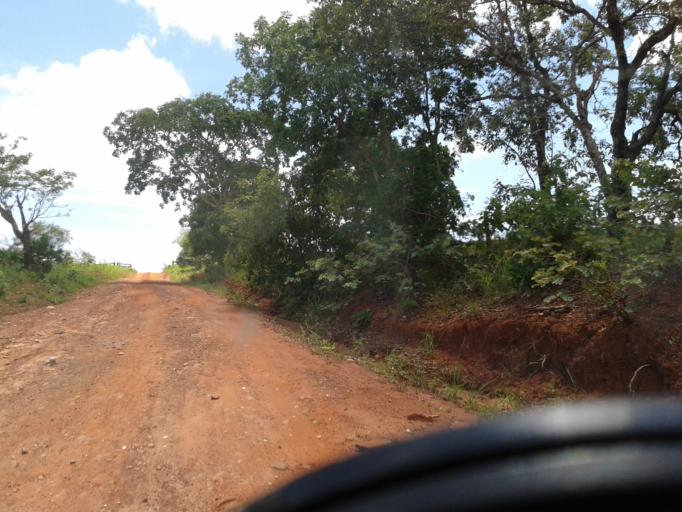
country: BR
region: Minas Gerais
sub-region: Santa Vitoria
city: Santa Vitoria
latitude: -18.9783
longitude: -49.8922
